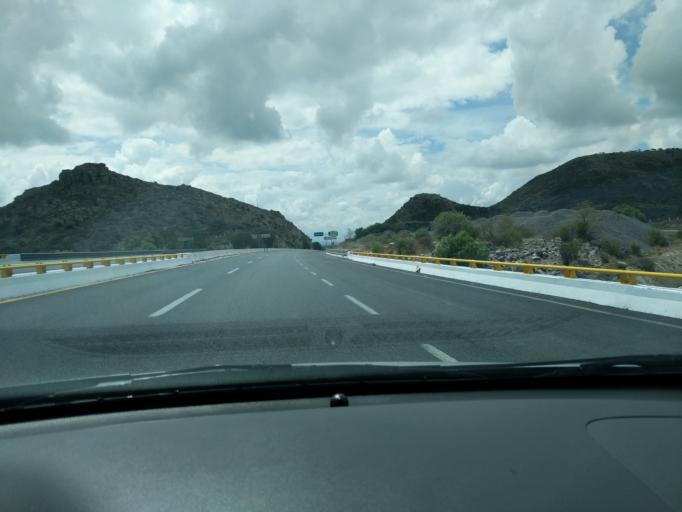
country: MX
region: San Luis Potosi
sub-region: Mexquitic de Carmona
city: Cerrito de Jaral
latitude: 22.2522
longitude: -101.1112
